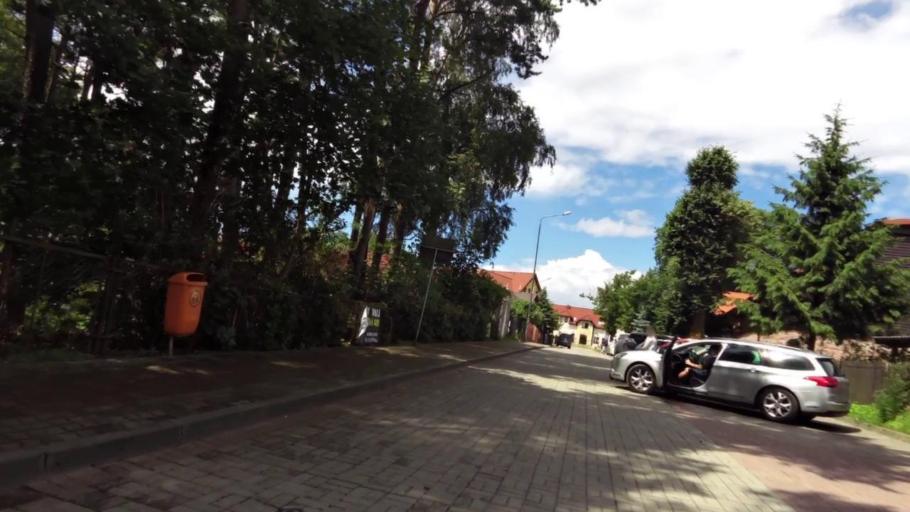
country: PL
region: West Pomeranian Voivodeship
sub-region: Powiat slawienski
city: Darlowo
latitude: 54.5378
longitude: 16.5289
